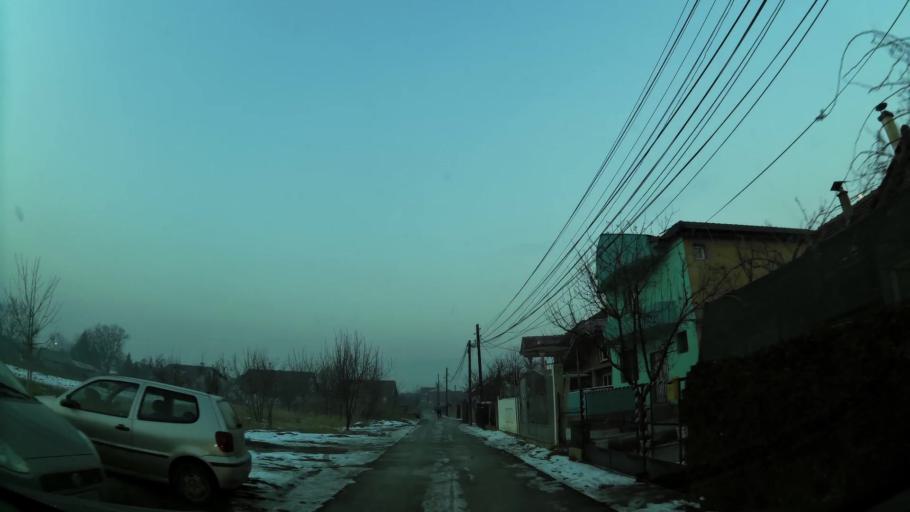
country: MK
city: Creshevo
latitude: 42.0001
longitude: 21.5093
